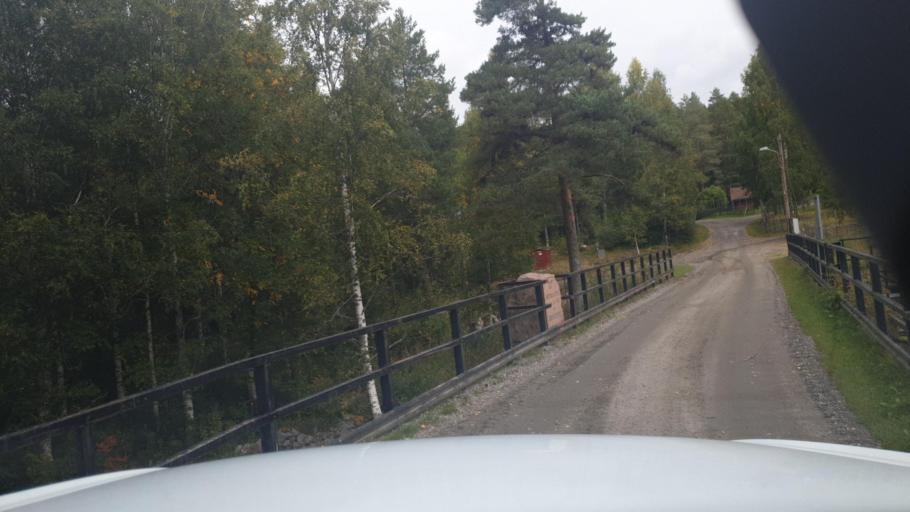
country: SE
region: Vaermland
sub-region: Eda Kommun
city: Charlottenberg
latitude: 60.0906
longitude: 12.5129
